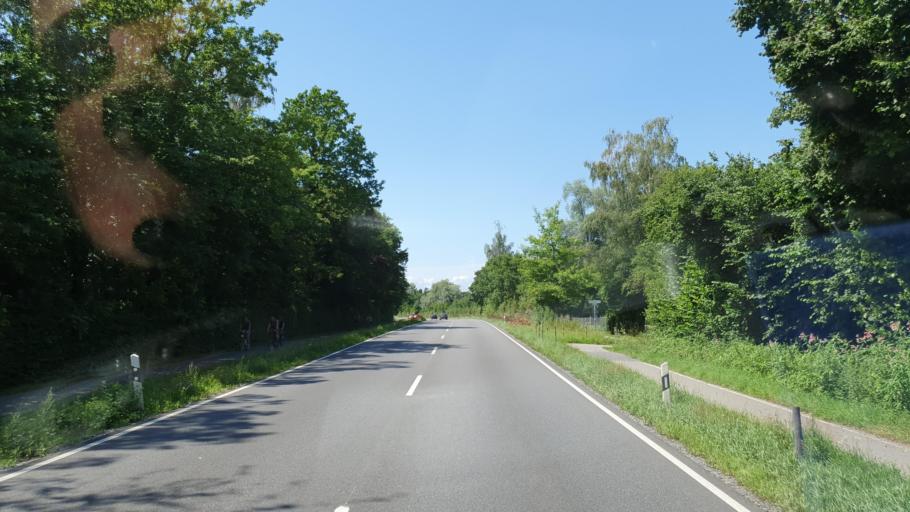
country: DE
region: Baden-Wuerttemberg
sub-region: Tuebingen Region
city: Immenstaad am Bodensee
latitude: 47.6710
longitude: 9.3900
